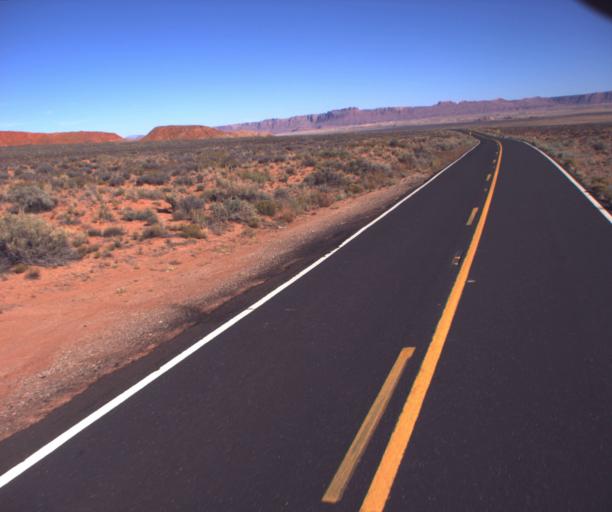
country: US
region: Arizona
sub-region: Coconino County
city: Page
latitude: 36.6837
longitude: -111.8537
